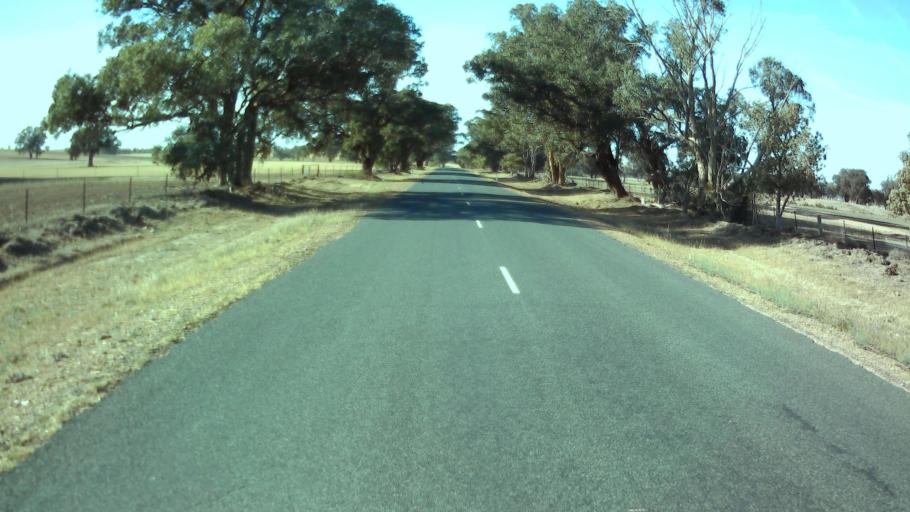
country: AU
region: New South Wales
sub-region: Weddin
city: Grenfell
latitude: -33.9603
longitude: 148.1400
